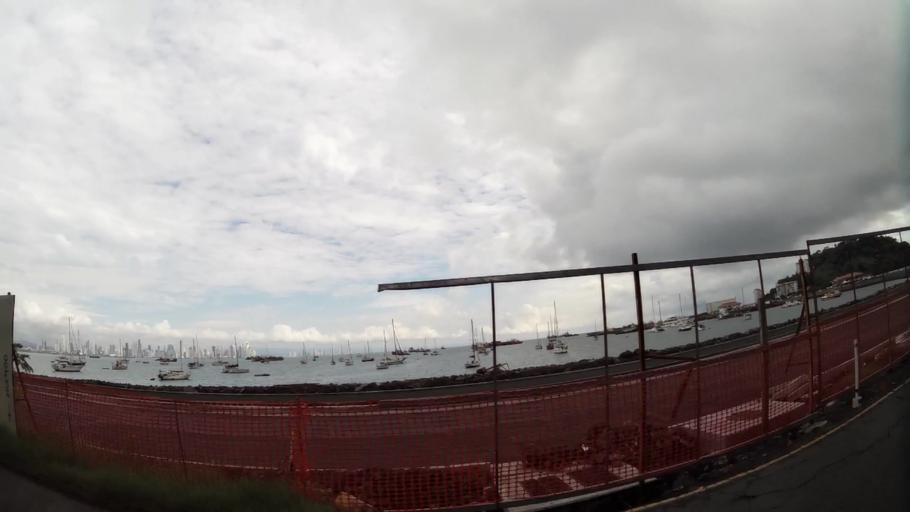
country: PA
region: Panama
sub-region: Distrito de Panama
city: Ancon
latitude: 8.9163
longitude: -79.5321
